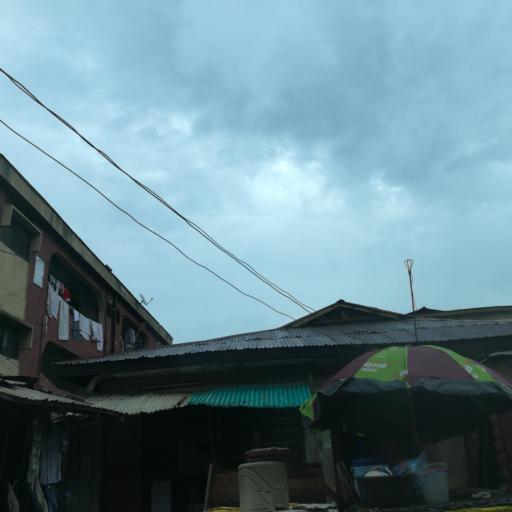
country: NG
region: Lagos
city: Oshodi
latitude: 6.5558
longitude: 3.3486
